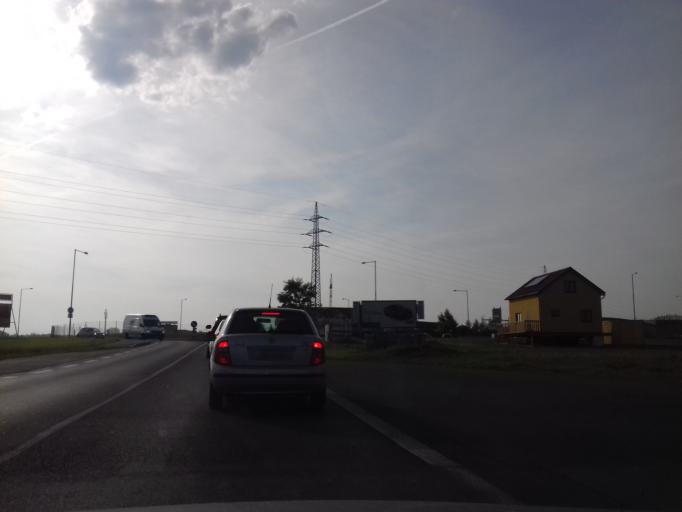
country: CZ
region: Central Bohemia
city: Vestec
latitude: 49.9922
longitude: 14.4894
